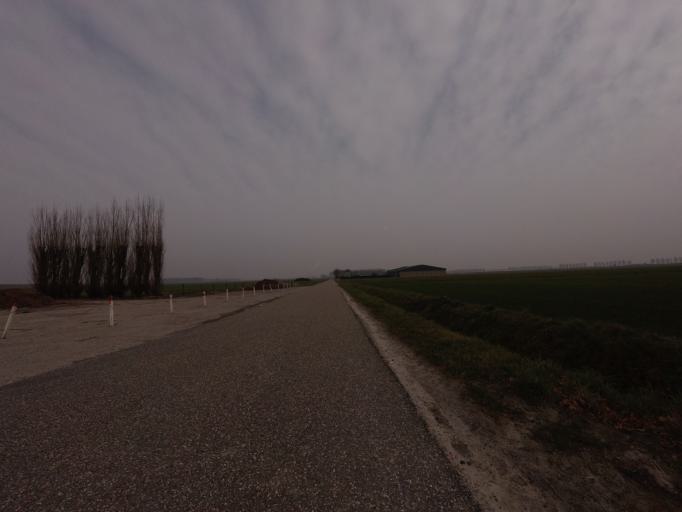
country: BE
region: Flanders
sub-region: Provincie Oost-Vlaanderen
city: Sint-Gillis-Waas
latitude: 51.3218
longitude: 4.1618
